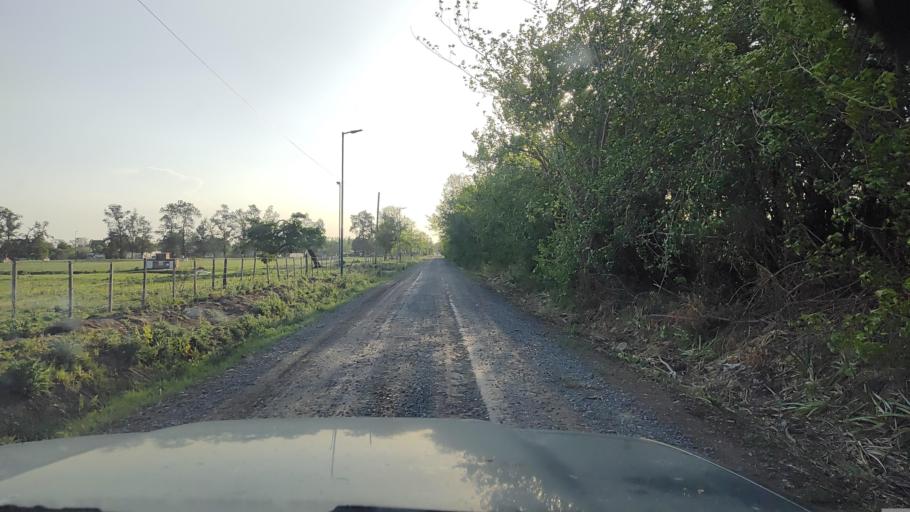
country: AR
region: Buenos Aires
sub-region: Partido de Lujan
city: Lujan
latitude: -34.5515
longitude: -59.1985
